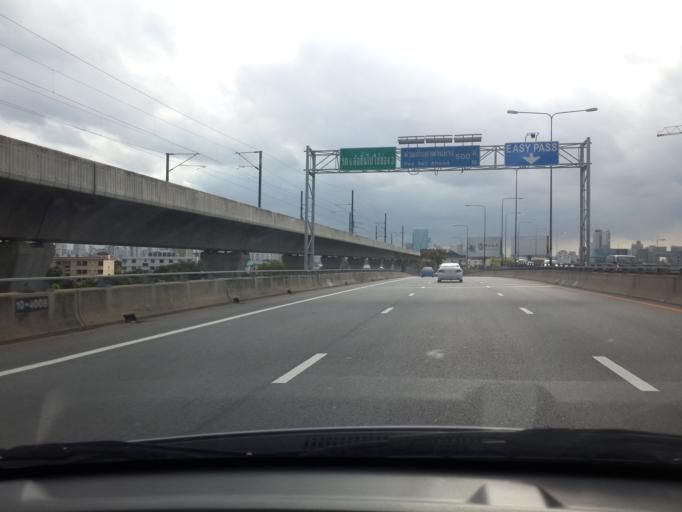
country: TH
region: Bangkok
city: Watthana
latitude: 13.7414
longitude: 100.6163
